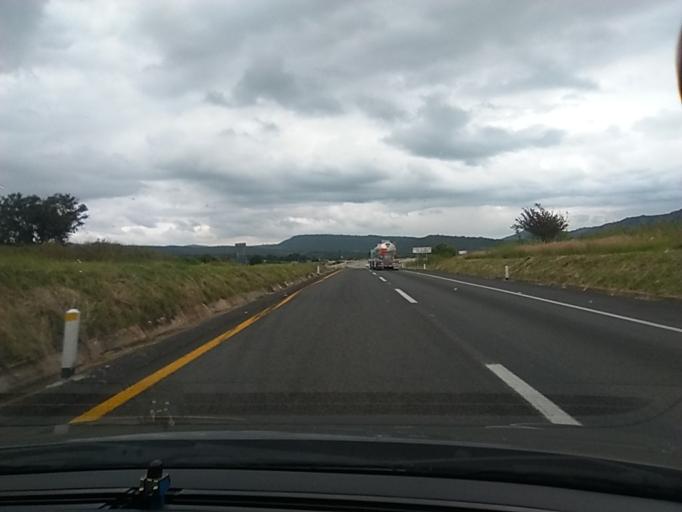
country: MX
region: Jalisco
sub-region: Zapotlanejo
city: La Mezquitera
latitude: 20.5486
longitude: -103.0367
